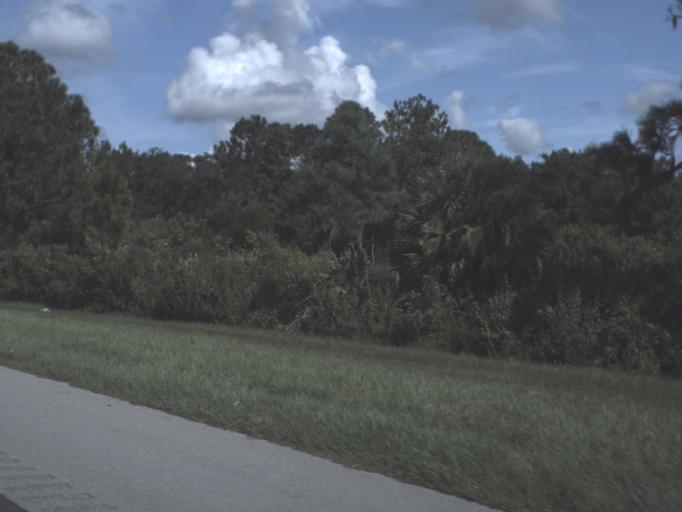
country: US
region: Florida
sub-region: Sarasota County
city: Nokomis
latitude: 27.1474
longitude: -82.4152
